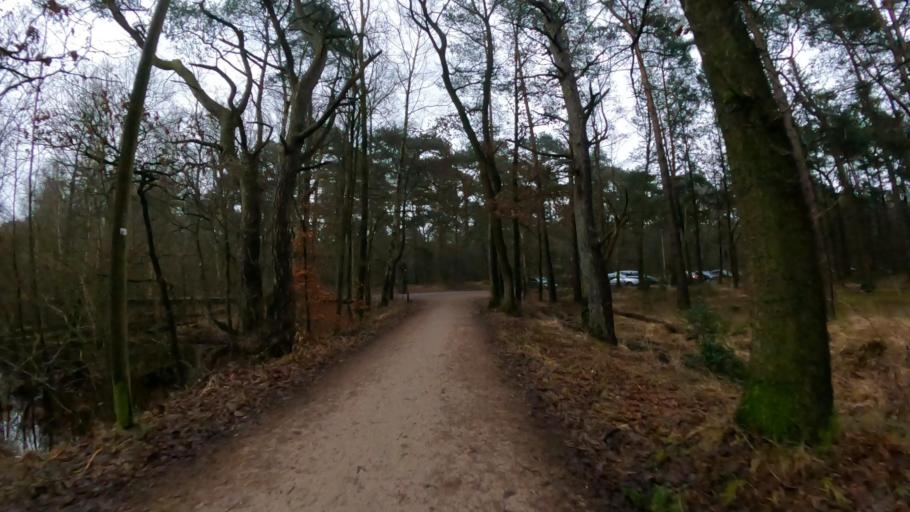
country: DE
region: Schleswig-Holstein
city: Appen
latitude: 53.6008
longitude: 9.7654
